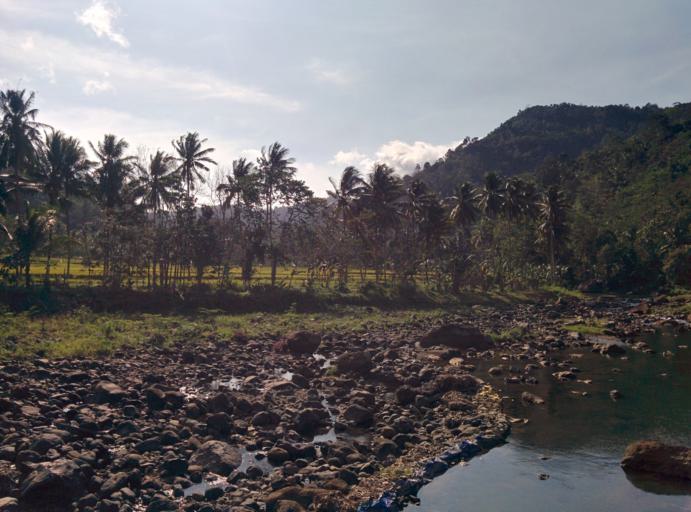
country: ID
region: East Java
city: Kedungbanteng Krajan
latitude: -8.3522
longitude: 112.7085
